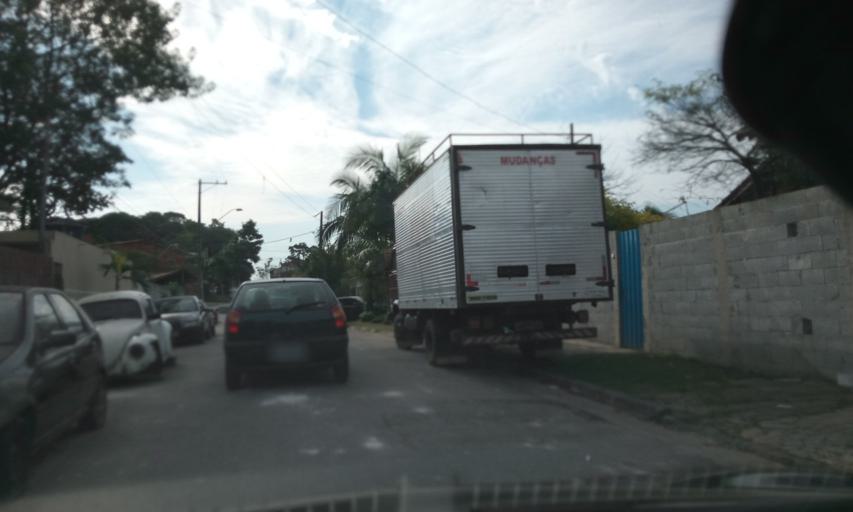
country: BR
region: Sao Paulo
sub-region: Sao Bernardo Do Campo
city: Sao Bernardo do Campo
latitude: -23.8016
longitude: -46.5383
